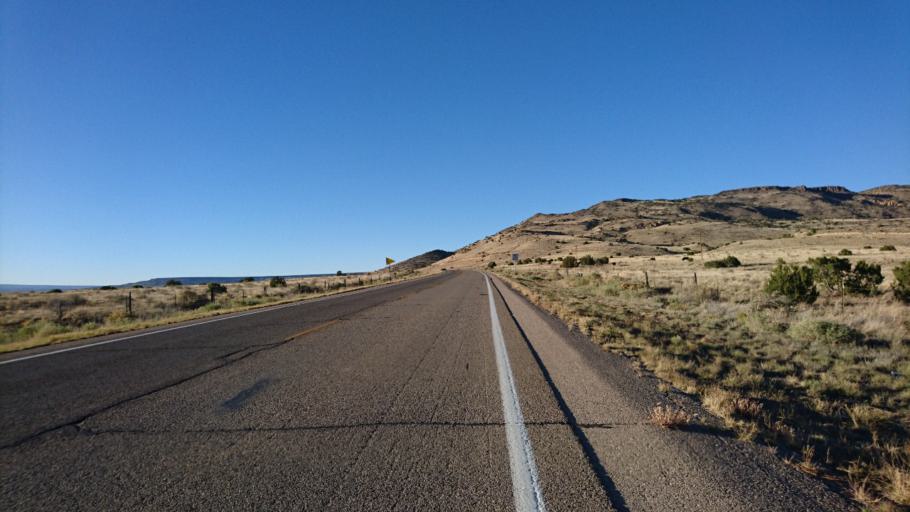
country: US
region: New Mexico
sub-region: Cibola County
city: Grants
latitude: 35.1099
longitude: -107.7816
